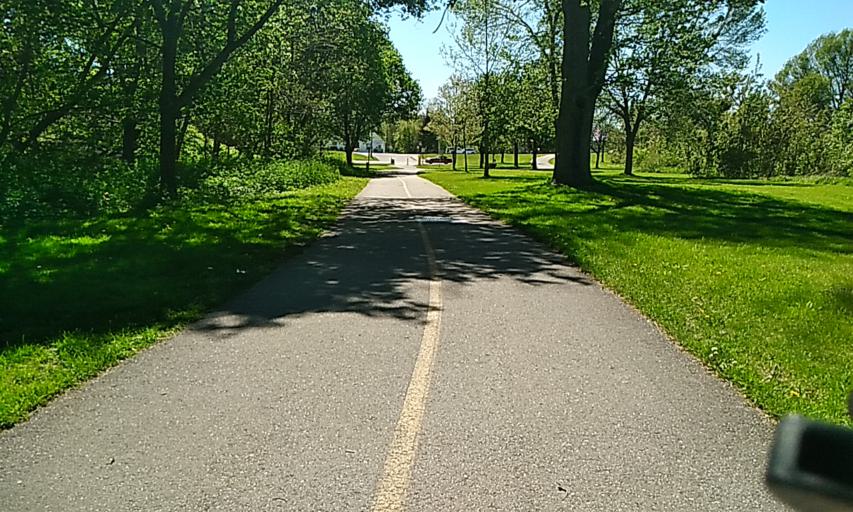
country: CA
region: Ontario
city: London
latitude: 42.9737
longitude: -81.2372
